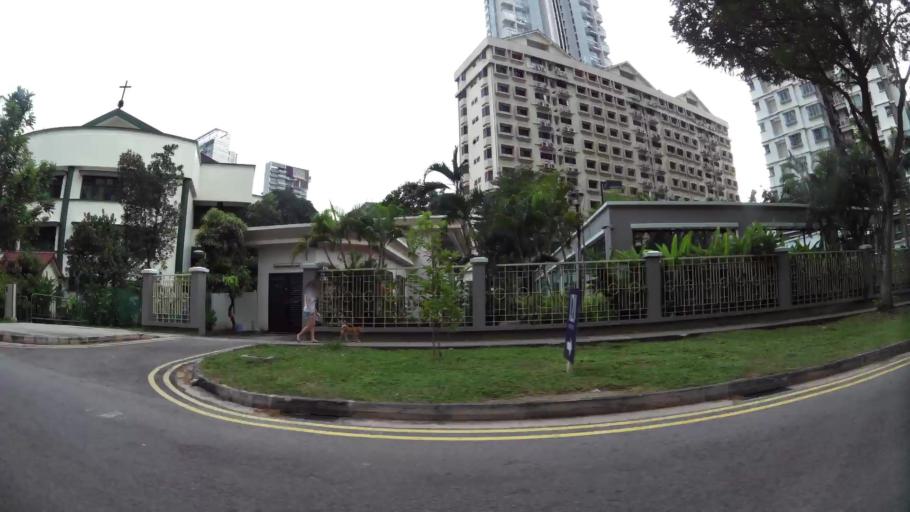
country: SG
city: Singapore
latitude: 1.3183
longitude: 103.8452
